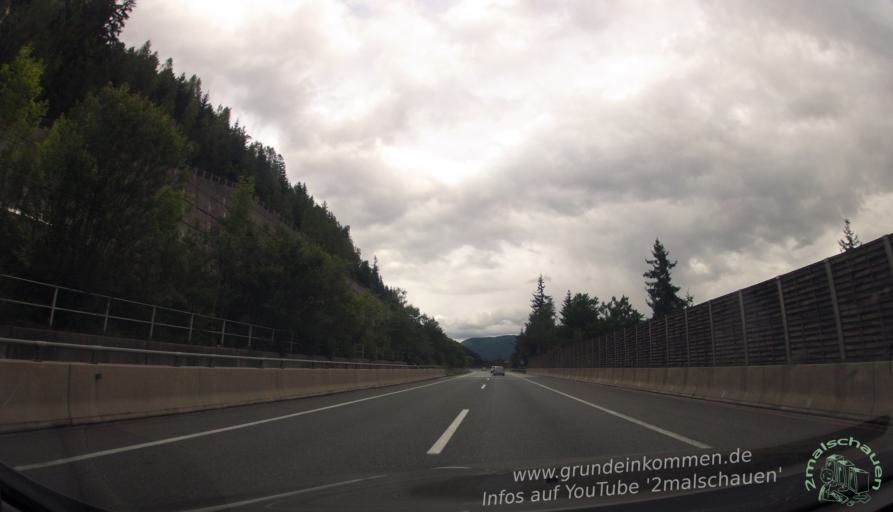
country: AT
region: Salzburg
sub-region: Politischer Bezirk Sankt Johann im Pongau
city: Huttau
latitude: 47.4318
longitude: 13.2788
